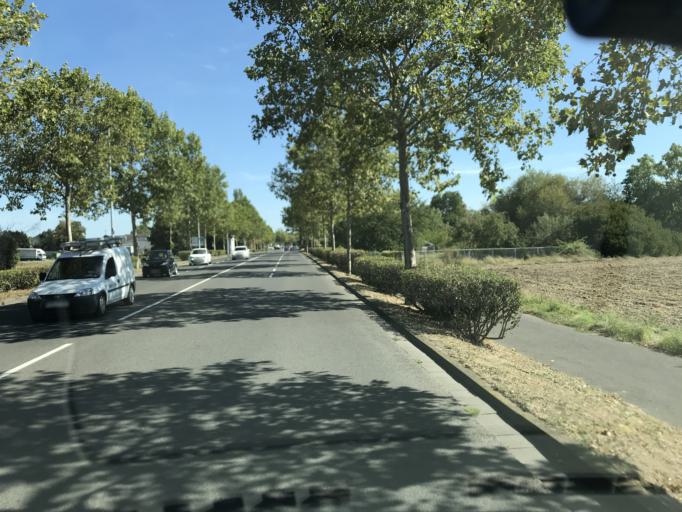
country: DE
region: Rheinland-Pfalz
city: Mainz
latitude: 50.0215
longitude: 8.2835
